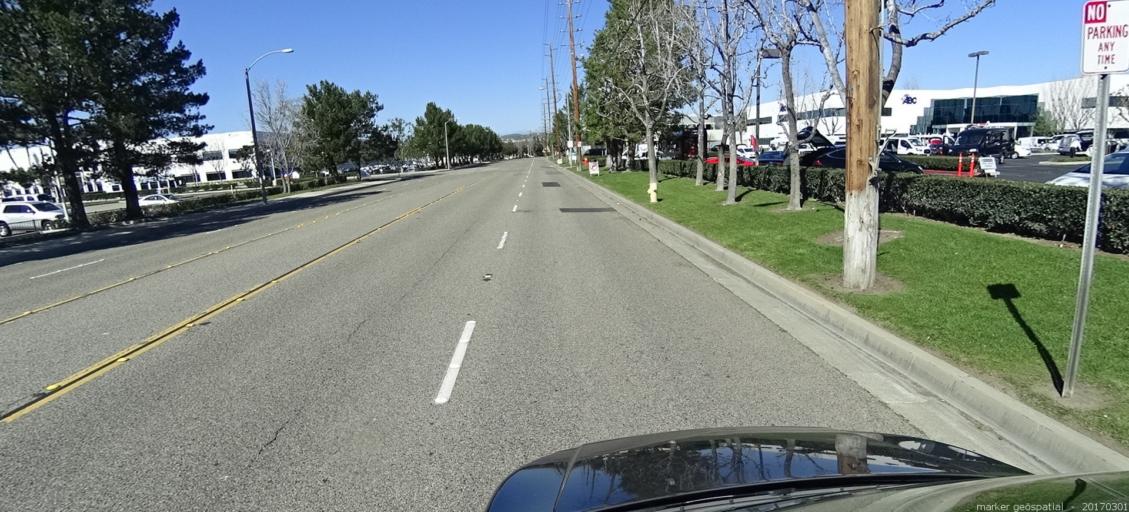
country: US
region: California
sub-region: Orange County
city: Yorba Linda
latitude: 33.8609
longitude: -117.8066
